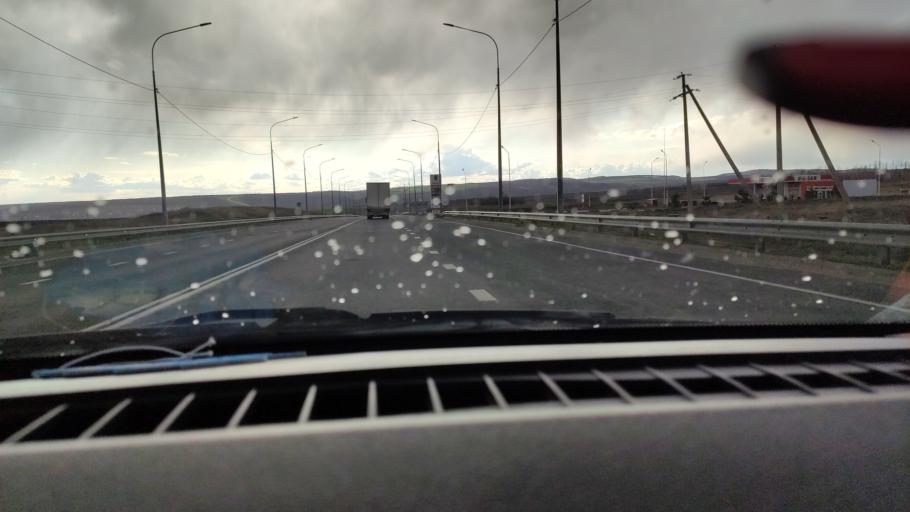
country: RU
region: Saratov
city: Yelshanka
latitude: 51.8304
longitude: 46.4249
